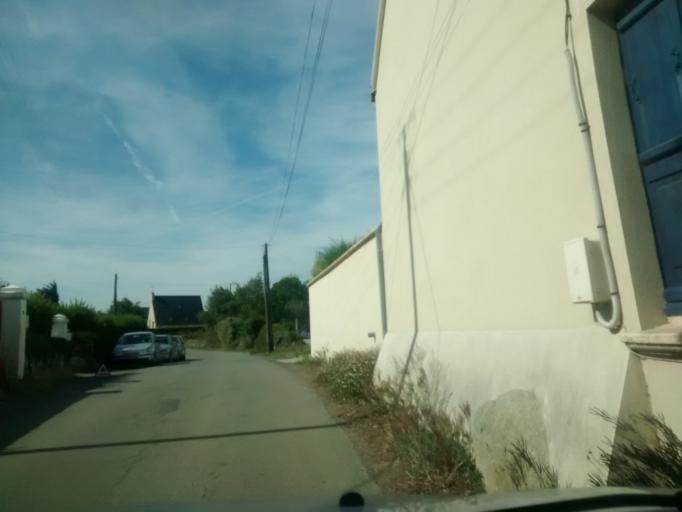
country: FR
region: Brittany
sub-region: Departement des Cotes-d'Armor
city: Plougrescant
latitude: 48.8535
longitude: -3.2335
